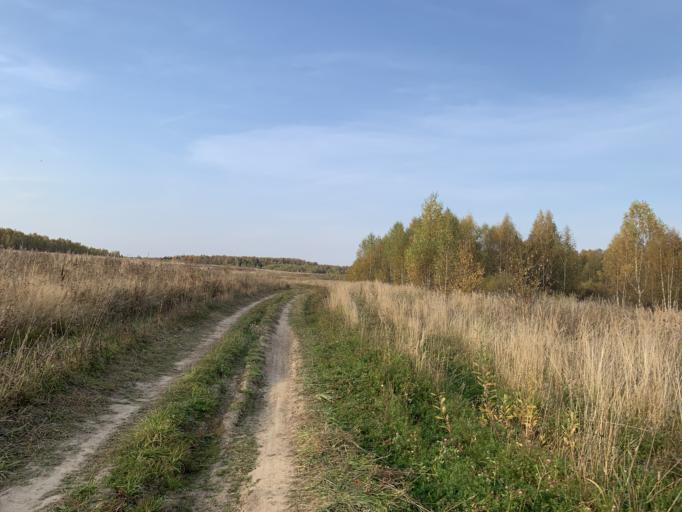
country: RU
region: Jaroslavl
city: Porech'ye-Rybnoye
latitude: 56.9821
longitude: 39.3842
